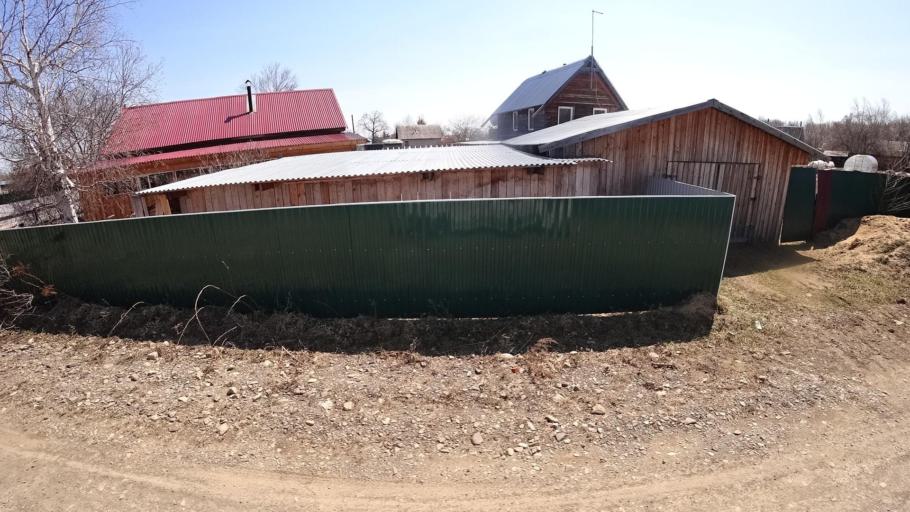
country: RU
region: Khabarovsk Krai
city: Khurba
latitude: 50.4110
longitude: 136.8618
